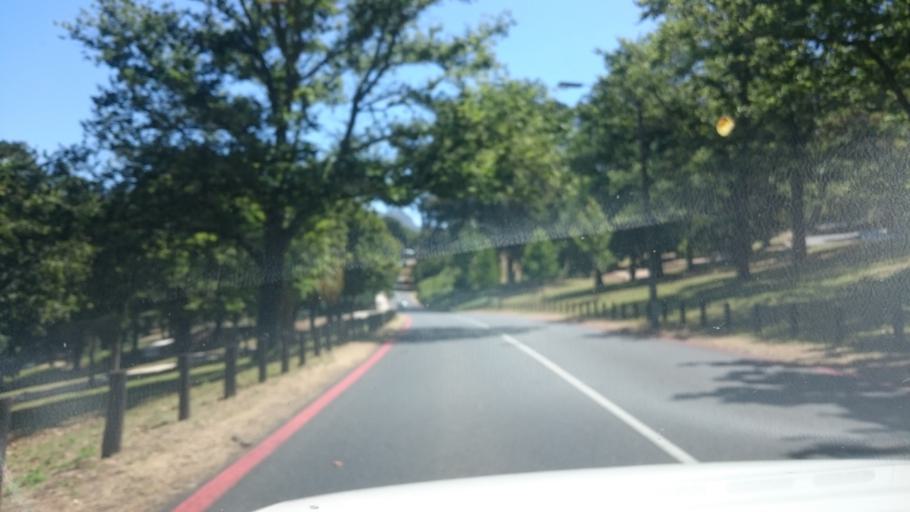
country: ZA
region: Western Cape
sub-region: City of Cape Town
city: Newlands
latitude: -33.9993
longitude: 18.4521
